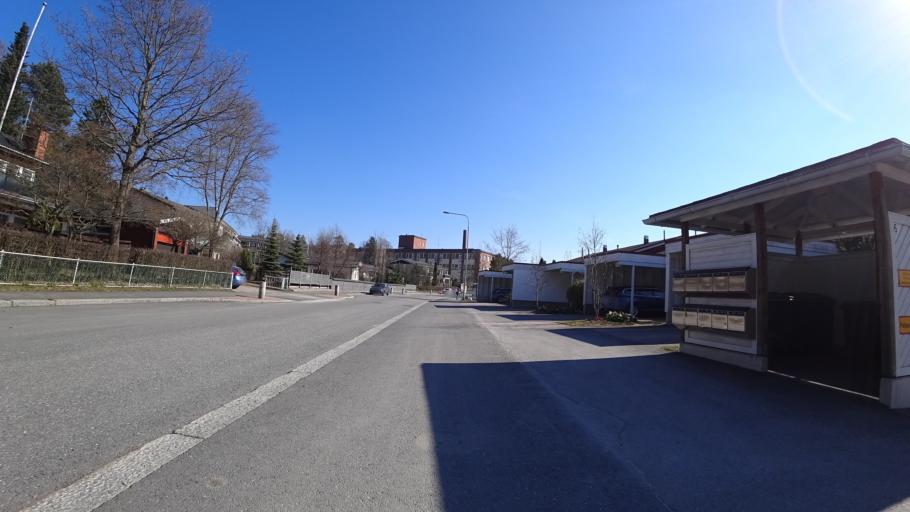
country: FI
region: Pirkanmaa
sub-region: Tampere
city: Pirkkala
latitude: 61.5106
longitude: 23.6618
